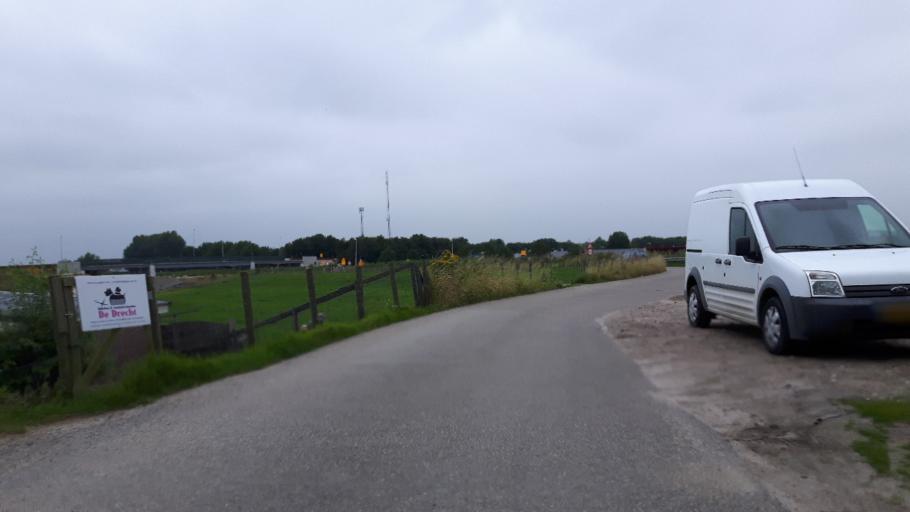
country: NL
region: South Holland
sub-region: Gemeente Kaag en Braassem
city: Leimuiden
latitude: 52.2212
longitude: 4.6830
